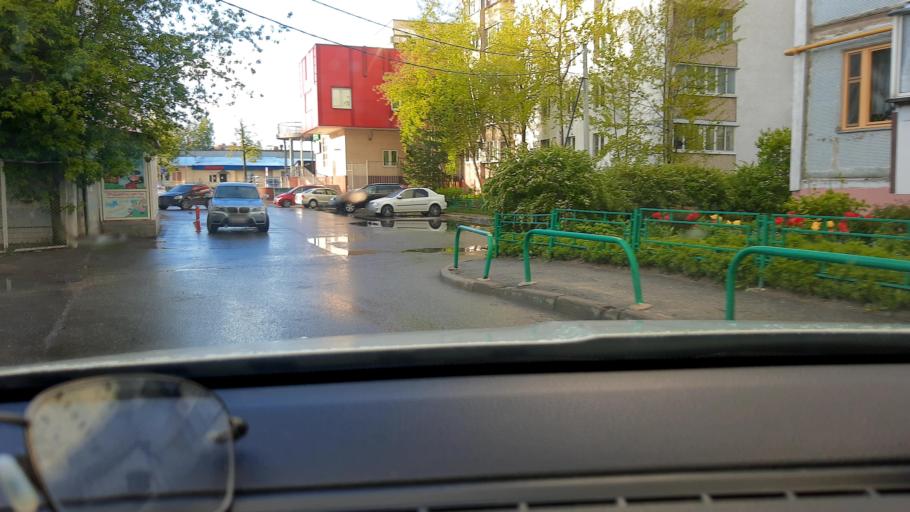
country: RU
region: Moskovskaya
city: Nakhabino
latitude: 55.8395
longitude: 37.1763
